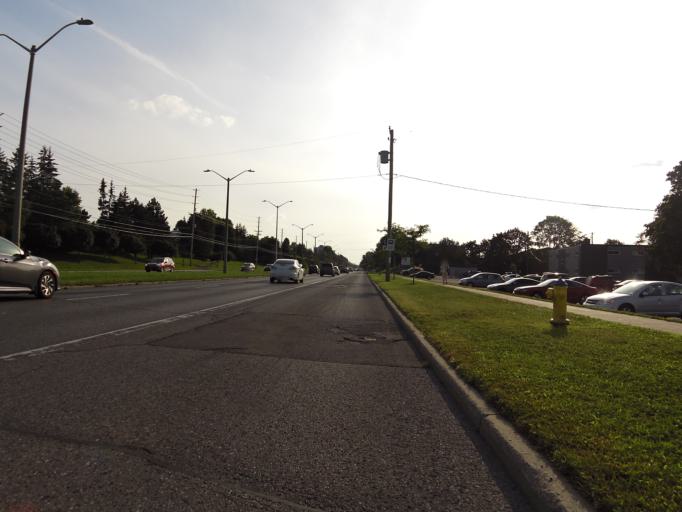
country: CA
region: Ontario
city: Bells Corners
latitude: 45.3484
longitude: -75.7705
